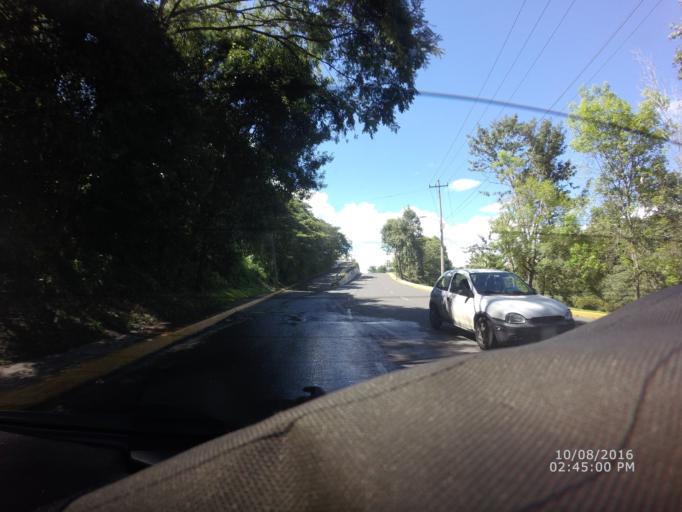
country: MX
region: Veracruz
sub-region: Xalapa
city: Lomas Verdes
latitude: 19.5066
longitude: -96.8990
